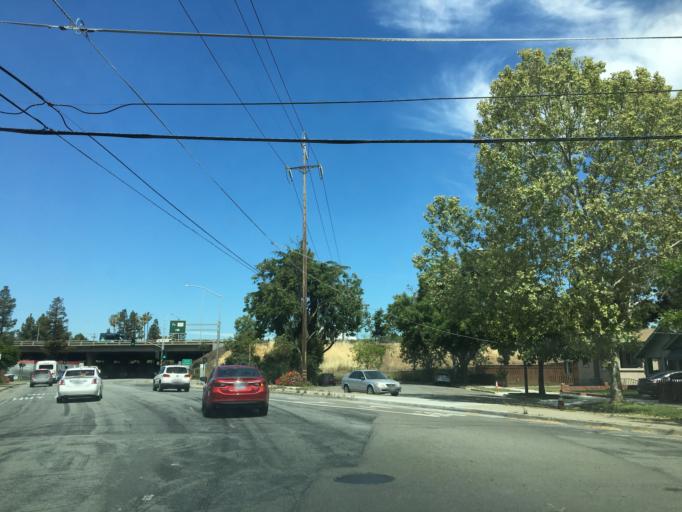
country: US
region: California
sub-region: Santa Clara County
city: San Jose
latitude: 37.3276
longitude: -121.8699
